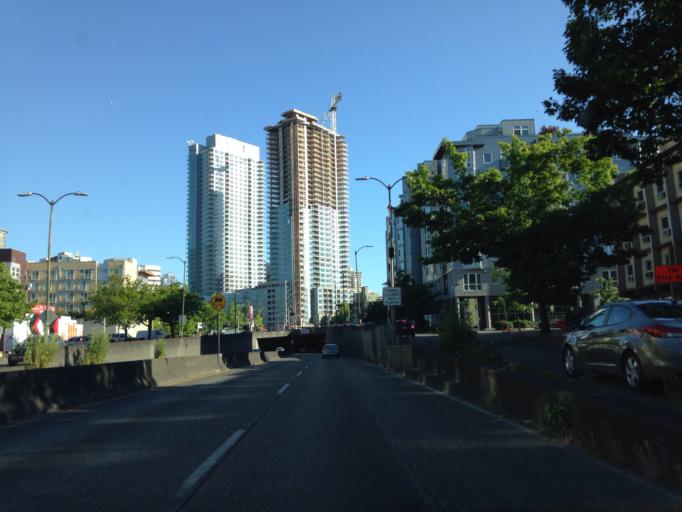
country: US
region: Washington
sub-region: King County
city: Seattle
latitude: 47.6204
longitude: -122.3438
